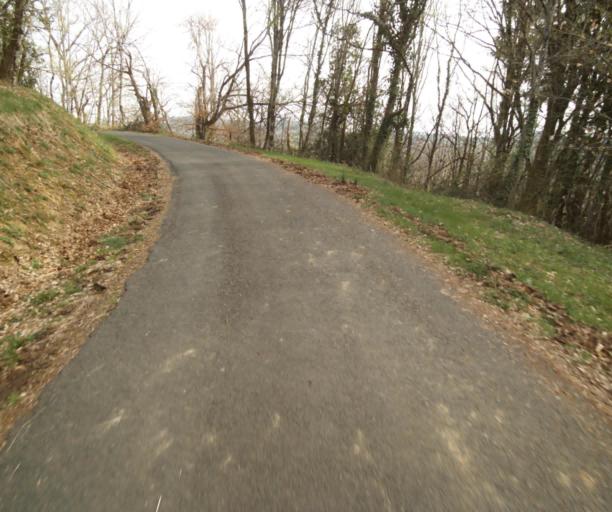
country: FR
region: Limousin
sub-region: Departement de la Correze
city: Seilhac
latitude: 45.4108
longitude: 1.7863
